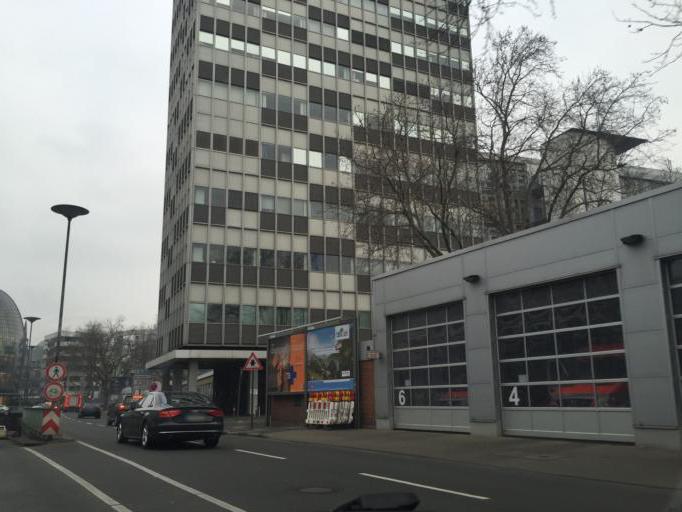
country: DE
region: North Rhine-Westphalia
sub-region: Regierungsbezirk Koln
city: Koeln
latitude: 50.9338
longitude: 6.9533
